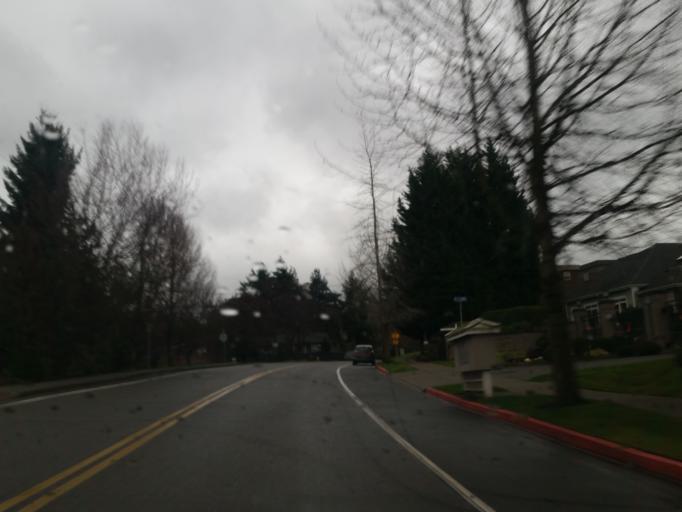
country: US
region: Washington
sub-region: King County
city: Kirkland
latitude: 47.6768
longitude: -122.1951
